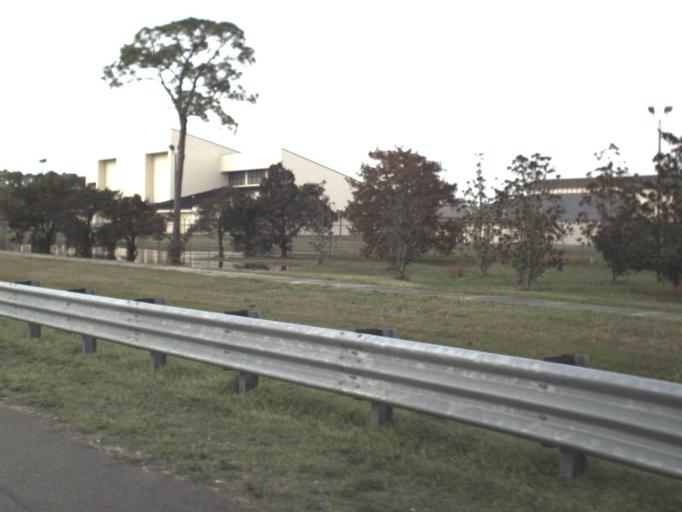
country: US
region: Florida
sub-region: Bay County
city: Tyndall Air Force Base
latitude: 30.0734
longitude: -85.5943
